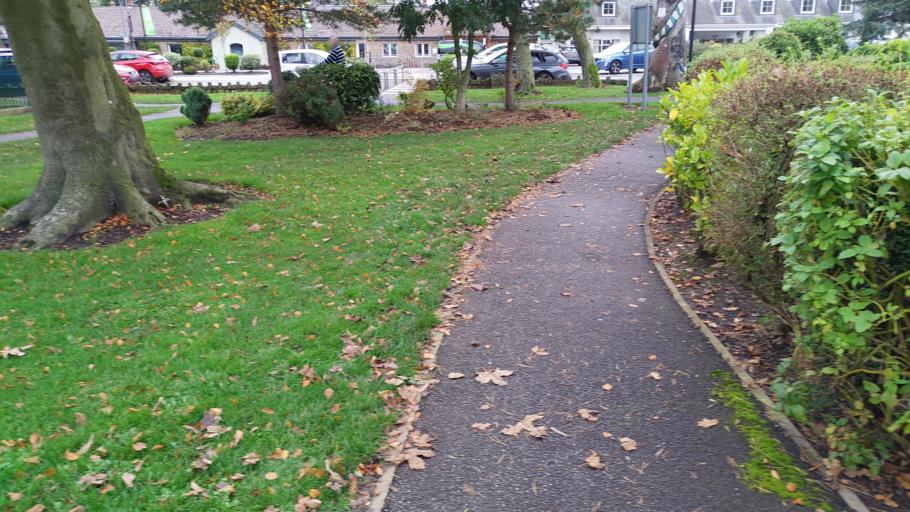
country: GB
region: England
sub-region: Lancashire
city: Kirkham
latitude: 53.7797
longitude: -2.8968
